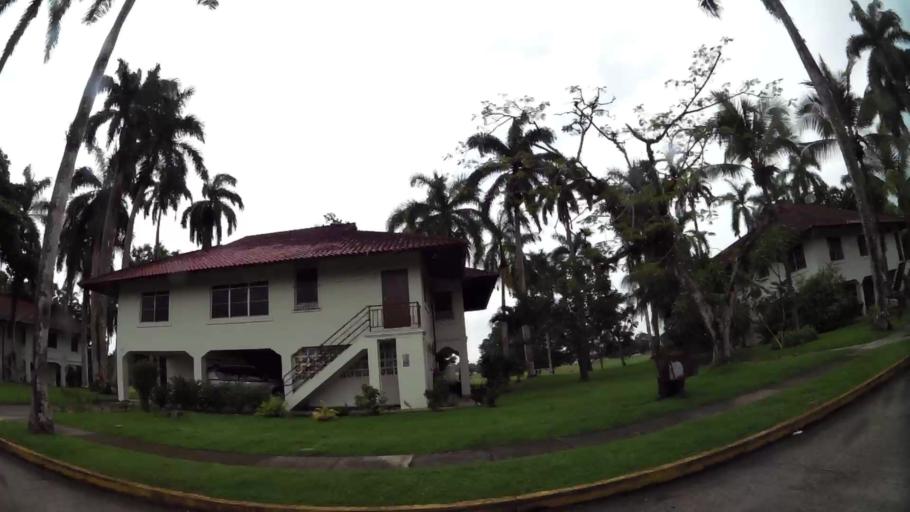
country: PA
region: Panama
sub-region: Distrito de Panama
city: Ancon
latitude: 9.0020
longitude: -79.5767
